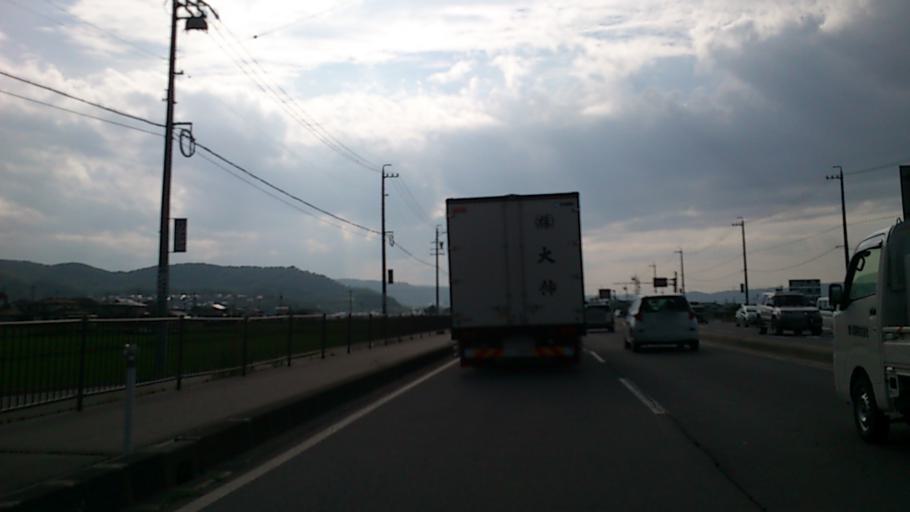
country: JP
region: Nagano
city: Saku
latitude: 36.2319
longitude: 138.4562
